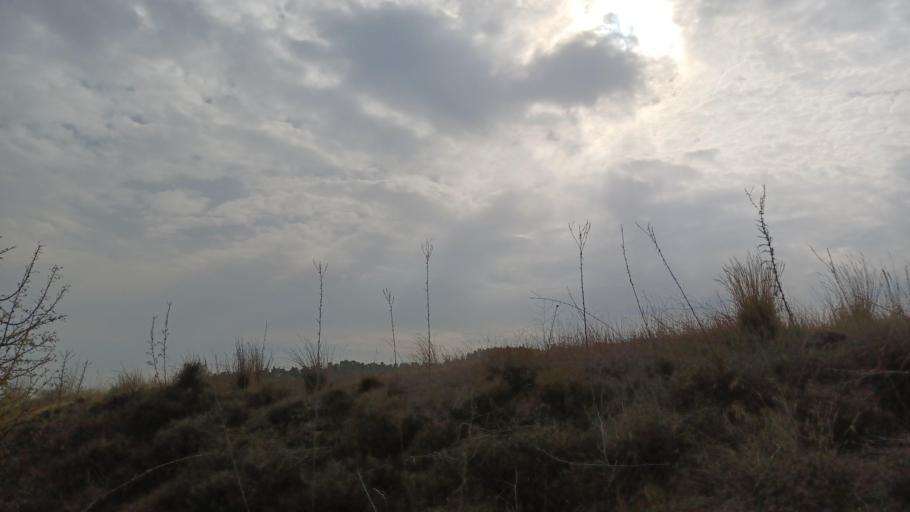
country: CY
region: Lefkosia
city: Klirou
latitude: 35.0403
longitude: 33.1102
